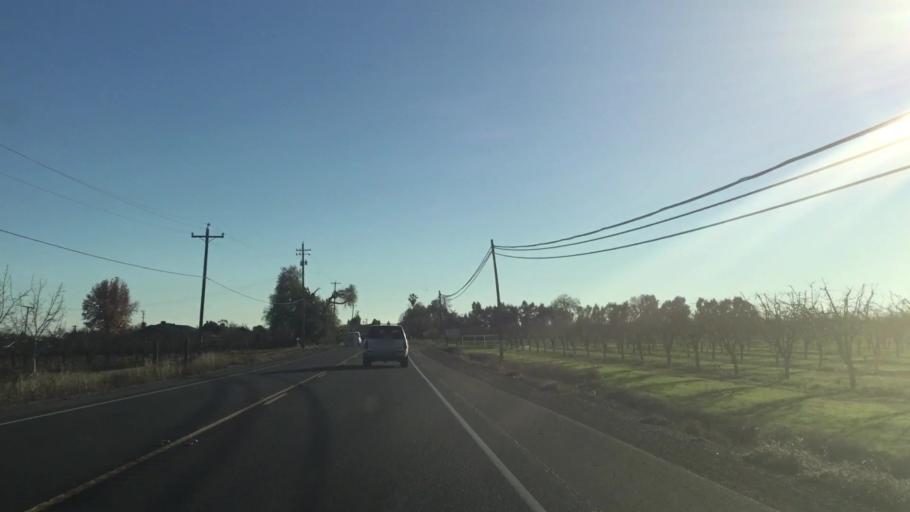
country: US
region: California
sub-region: Yuba County
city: Marysville
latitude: 39.2040
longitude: -121.5950
